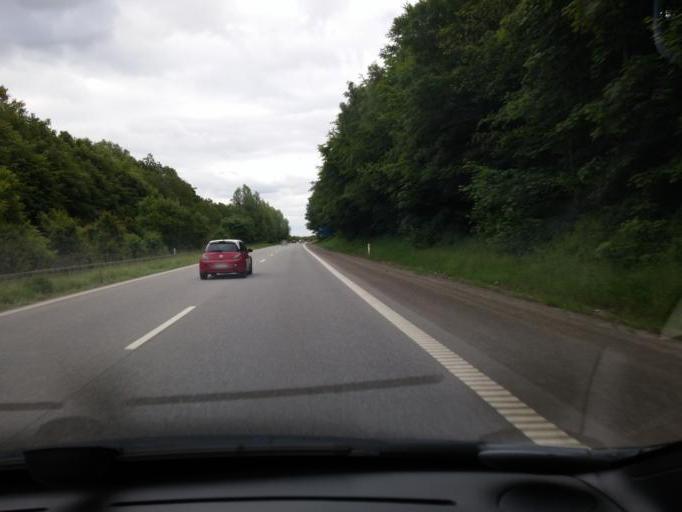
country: DK
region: Capital Region
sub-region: Fureso Kommune
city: Farum
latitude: 55.8351
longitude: 12.3610
